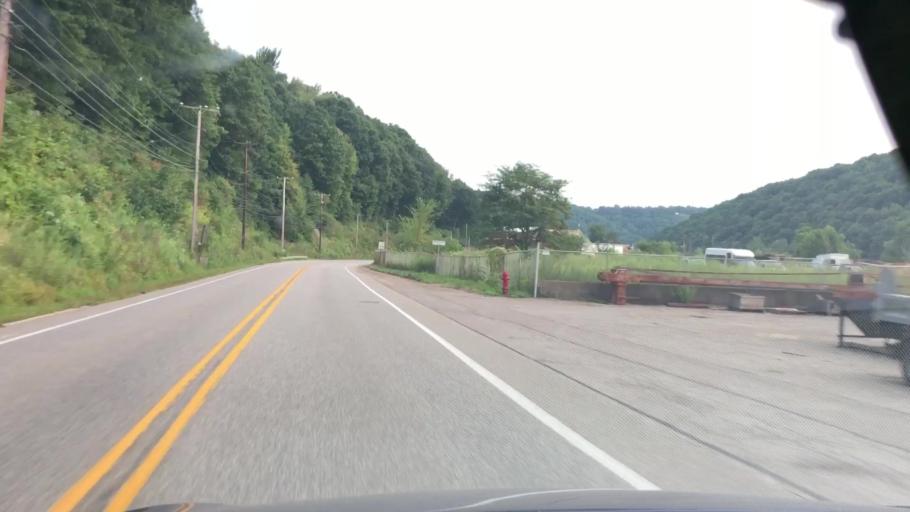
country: US
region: Pennsylvania
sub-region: Venango County
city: Hasson Heights
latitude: 41.4638
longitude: -79.6895
